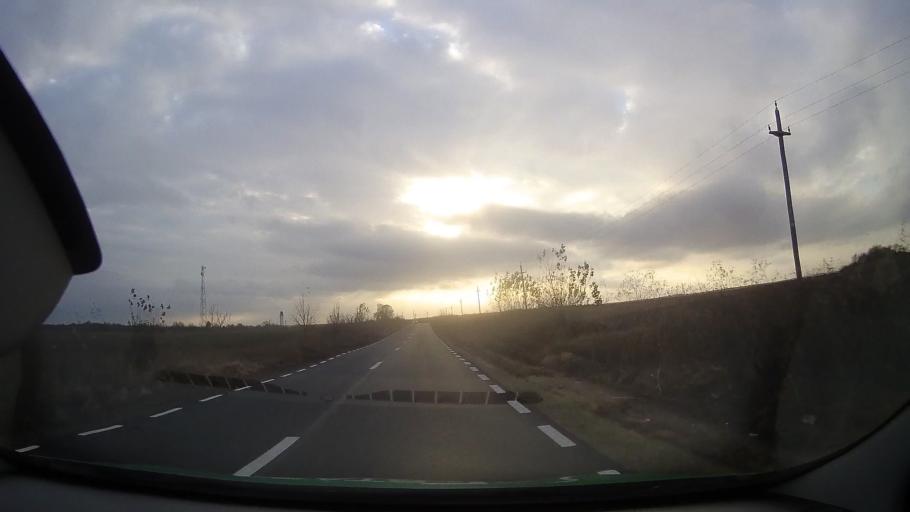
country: RO
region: Constanta
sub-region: Comuna Adamclisi
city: Adamclisi
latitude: 44.0698
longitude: 27.9801
